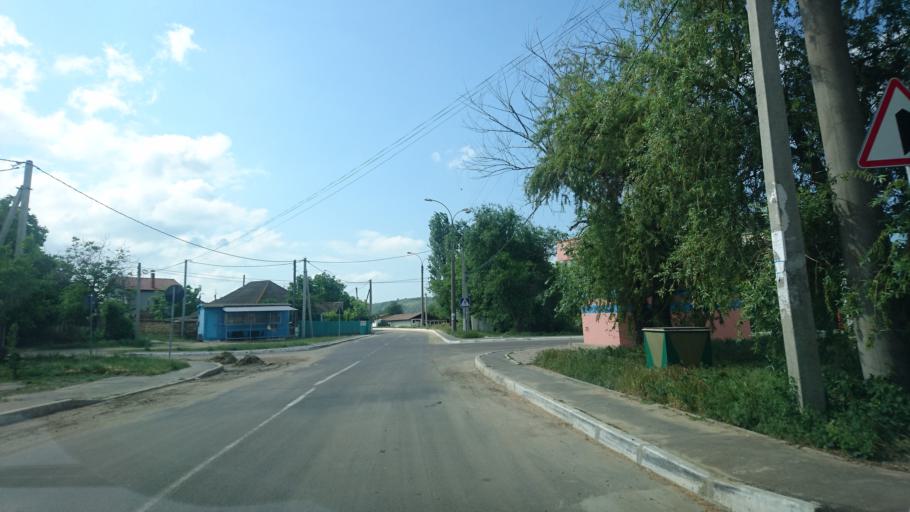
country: MD
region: Telenesti
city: Cocieri
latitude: 47.3512
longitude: 29.1079
